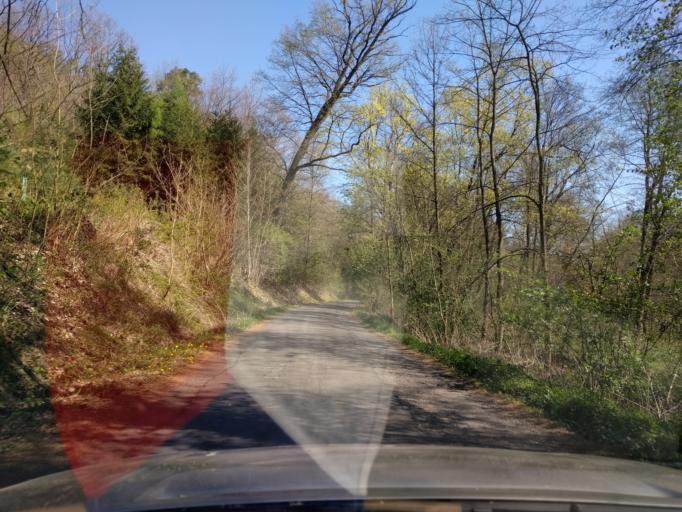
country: CZ
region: Central Bohemia
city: Cesky Brod
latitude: 50.0357
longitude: 14.8302
